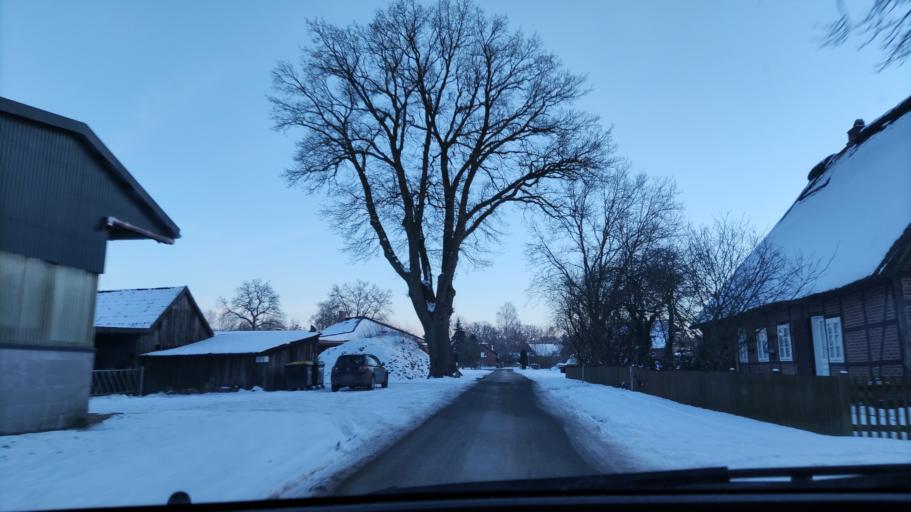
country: DE
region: Lower Saxony
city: Neetze
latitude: 53.2987
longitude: 10.6661
